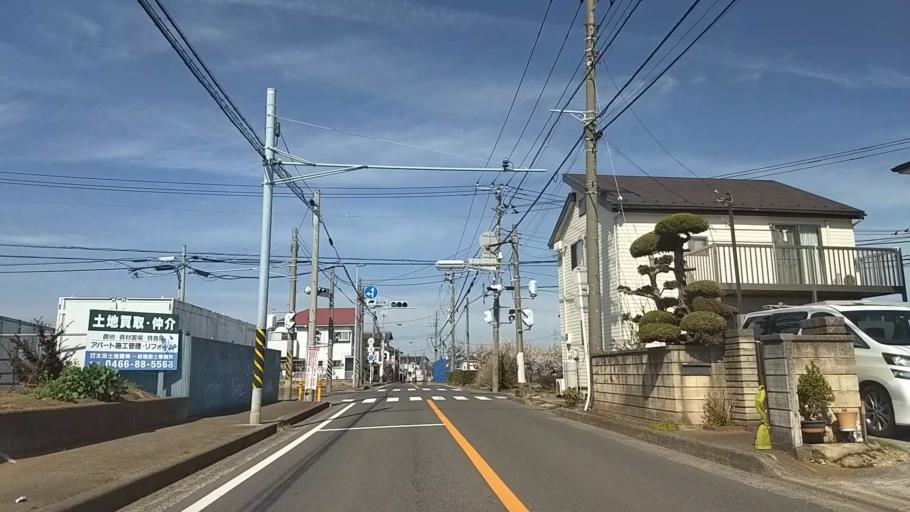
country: JP
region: Kanagawa
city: Fujisawa
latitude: 35.3817
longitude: 139.4377
